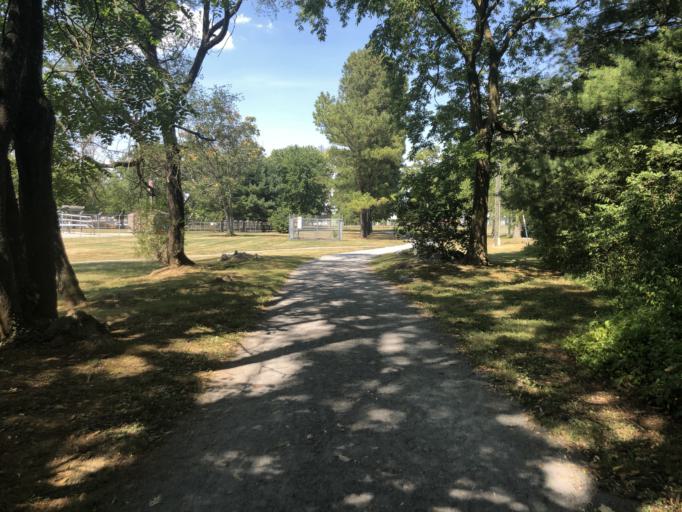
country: US
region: Virginia
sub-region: Clarke County
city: Berryville
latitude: 39.1626
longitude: -78.0007
